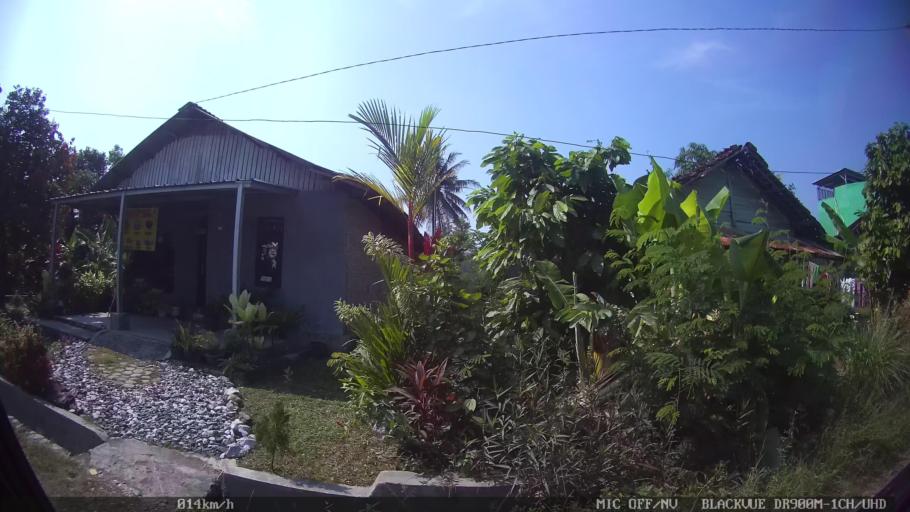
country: ID
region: Lampung
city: Natar
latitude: -5.2566
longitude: 105.1856
